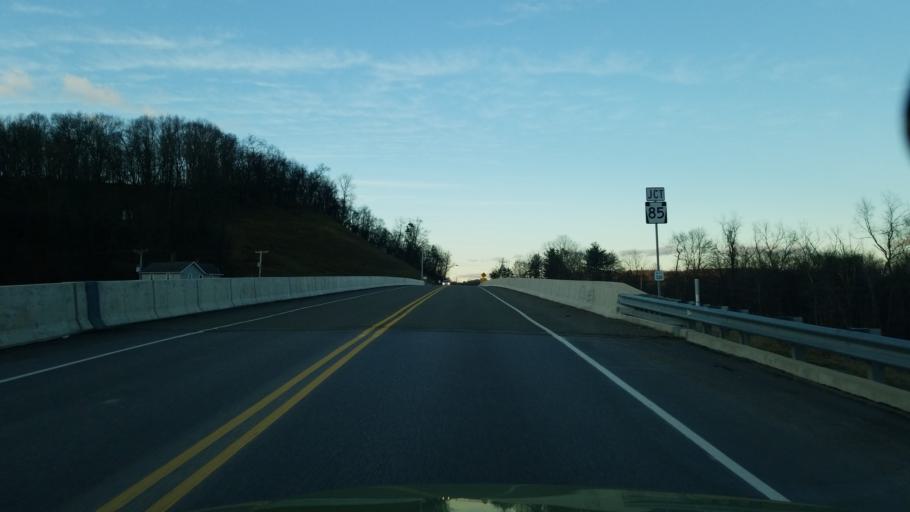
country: US
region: Pennsylvania
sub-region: Indiana County
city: Chevy Chase Heights
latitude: 40.7349
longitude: -79.1046
